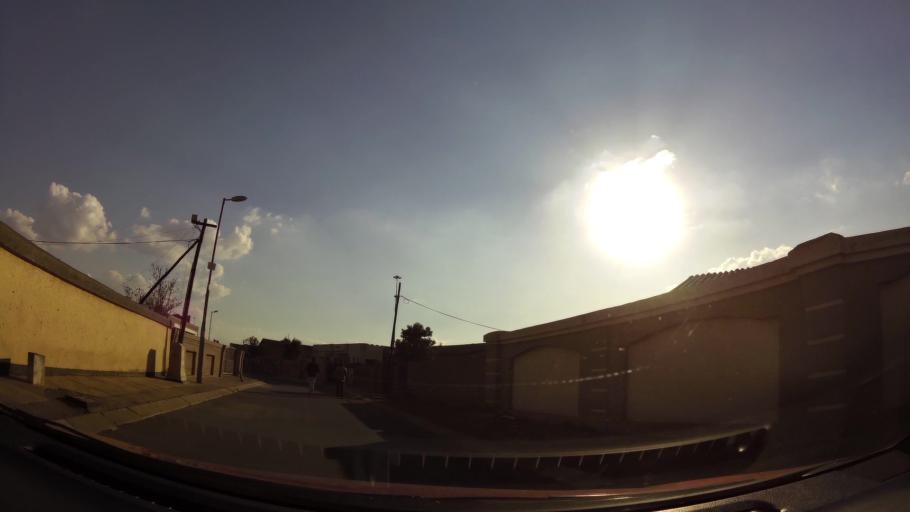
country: ZA
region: Gauteng
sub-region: City of Johannesburg Metropolitan Municipality
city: Soweto
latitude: -26.2372
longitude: 27.8562
